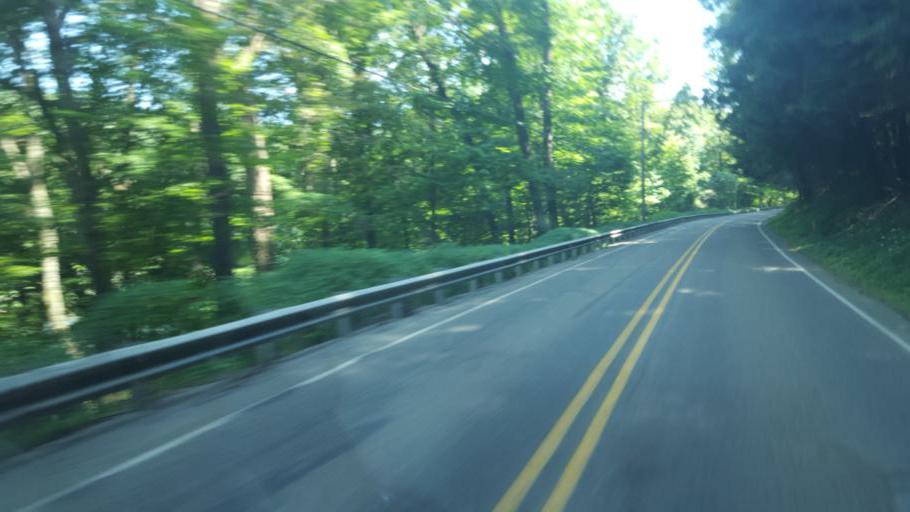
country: US
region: Pennsylvania
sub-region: Clarion County
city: Knox
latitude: 41.1635
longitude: -79.6831
